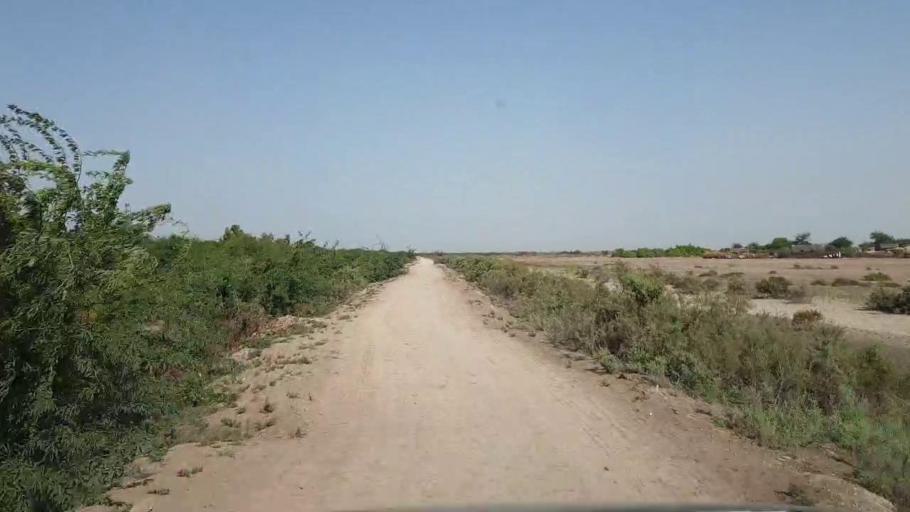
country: PK
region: Sindh
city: Tando Bago
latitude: 24.6486
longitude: 69.0714
